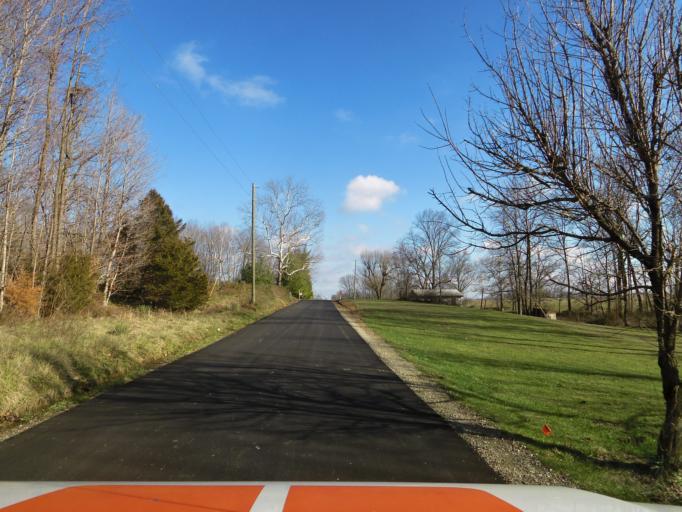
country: US
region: Indiana
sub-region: Jennings County
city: Country Squire Lakes
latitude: 38.9832
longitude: -85.7790
